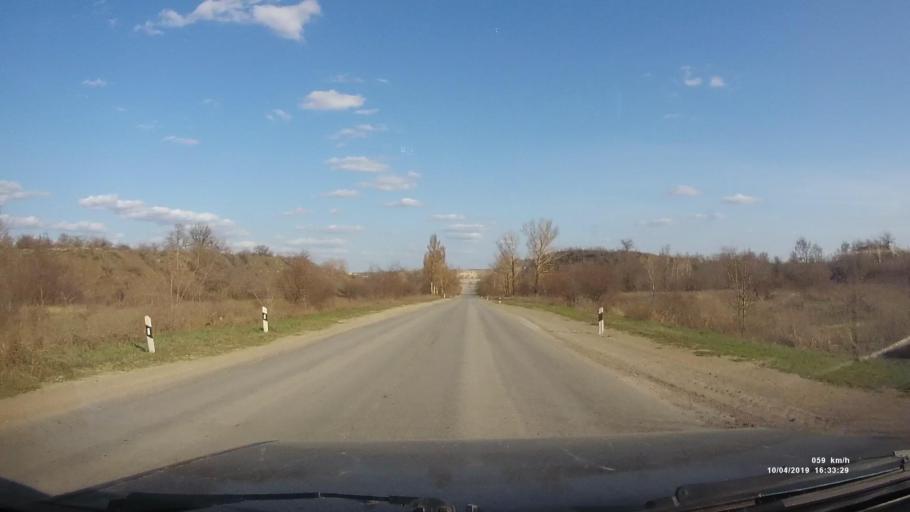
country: RU
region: Rostov
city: Staraya Stanitsa
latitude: 48.2410
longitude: 40.3981
